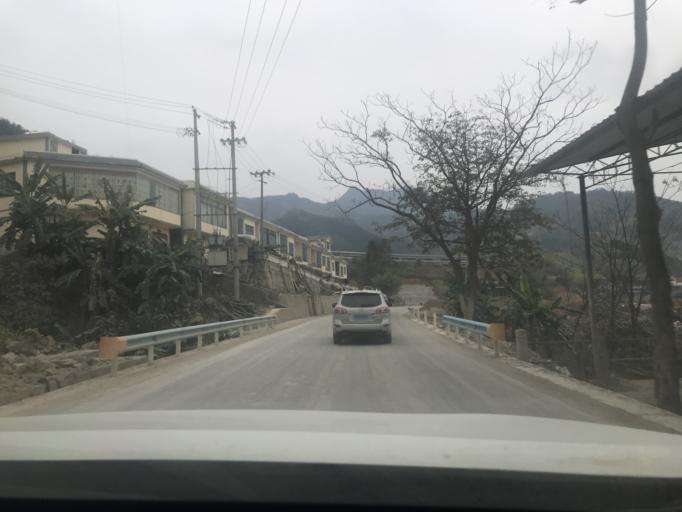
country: CN
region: Guangxi Zhuangzu Zizhiqu
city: Xinzhou
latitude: 25.0157
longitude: 105.8611
